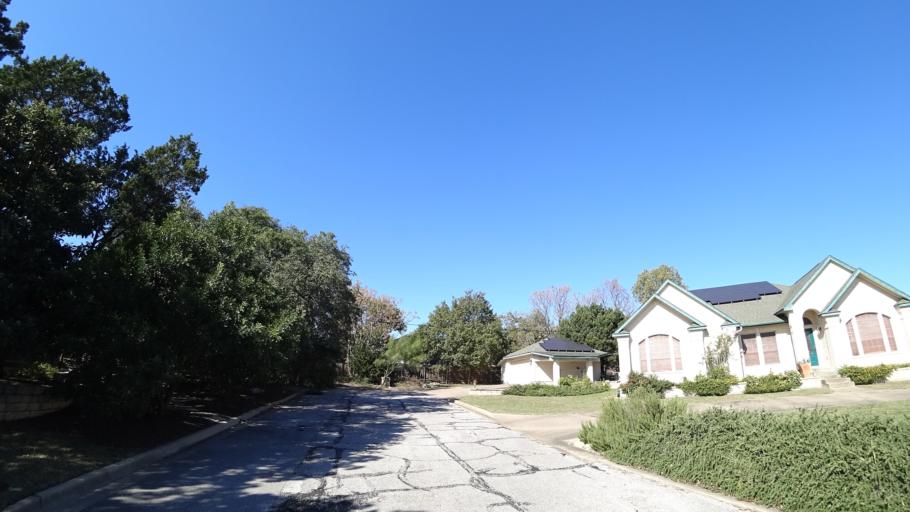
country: US
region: Texas
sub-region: Williamson County
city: Jollyville
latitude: 30.4127
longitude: -97.7552
